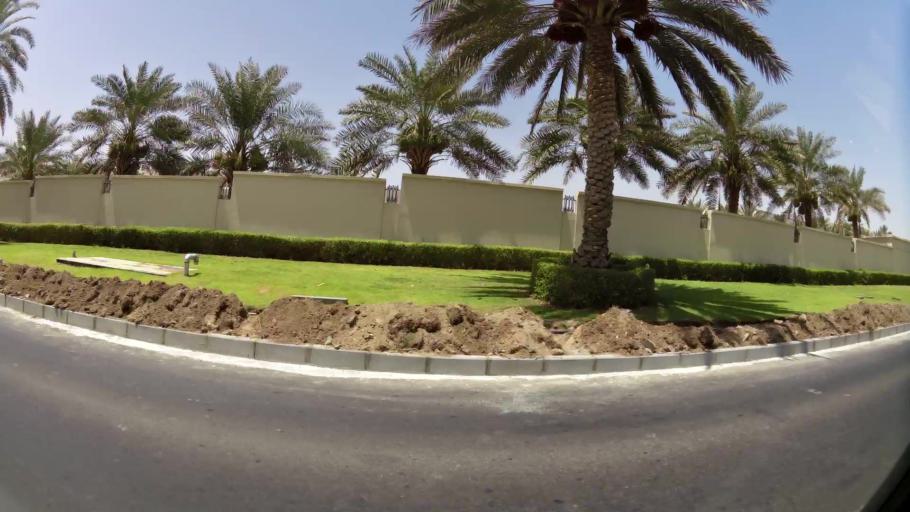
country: OM
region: Muhafazat Masqat
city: Bawshar
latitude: 23.5987
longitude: 58.4743
